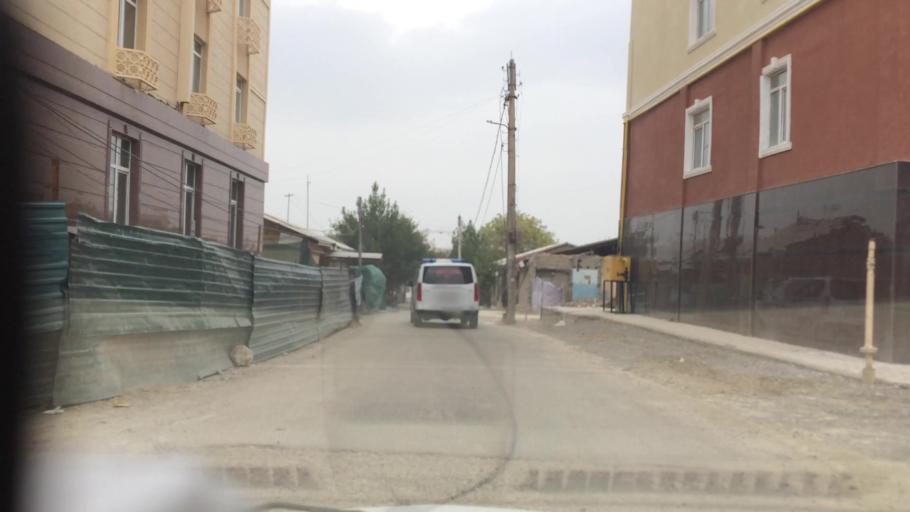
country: UZ
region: Toshkent
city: Salor
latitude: 41.3091
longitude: 69.3361
